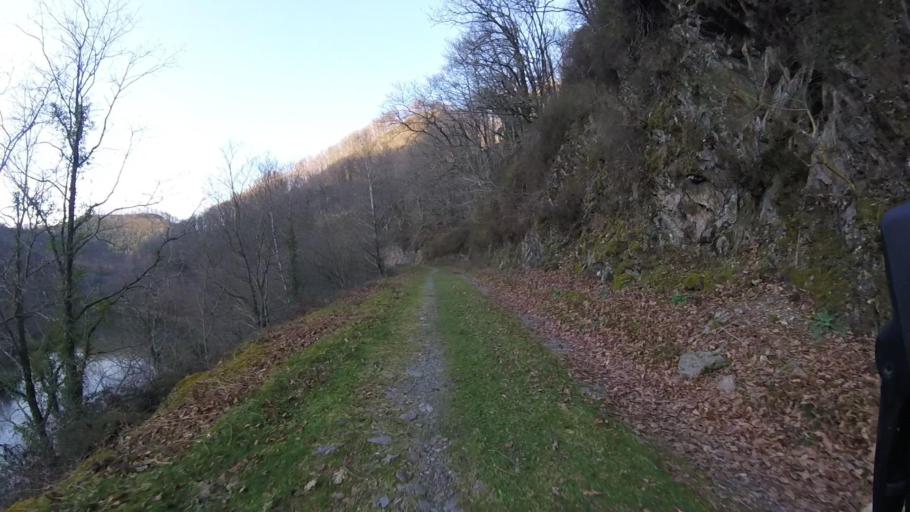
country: ES
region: Navarre
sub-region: Provincia de Navarra
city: Arano
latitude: 43.2155
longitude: -1.8627
